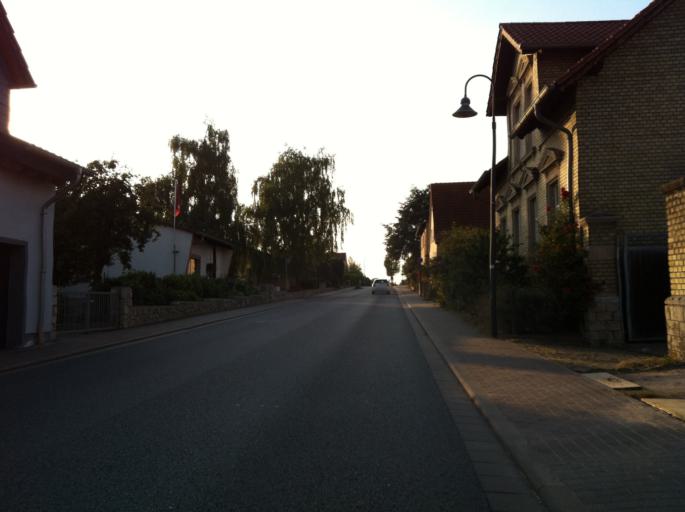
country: DE
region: Rheinland-Pfalz
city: Stadecken-Elsheim
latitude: 49.9170
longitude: 8.1221
